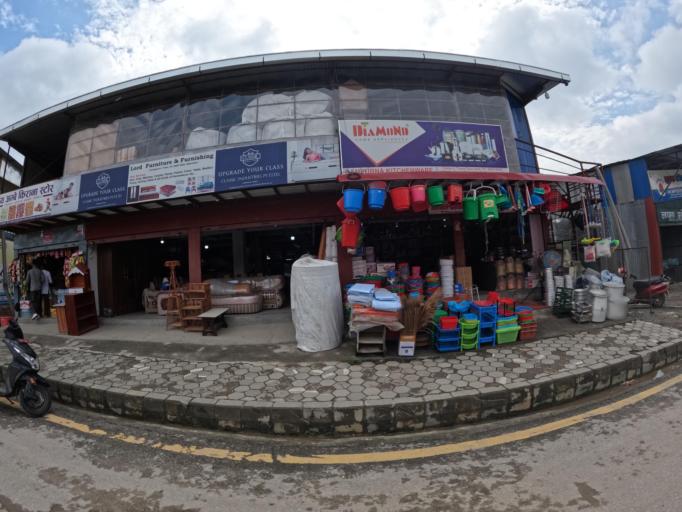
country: NP
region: Central Region
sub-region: Bagmati Zone
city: Kathmandu
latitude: 27.7613
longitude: 85.3170
